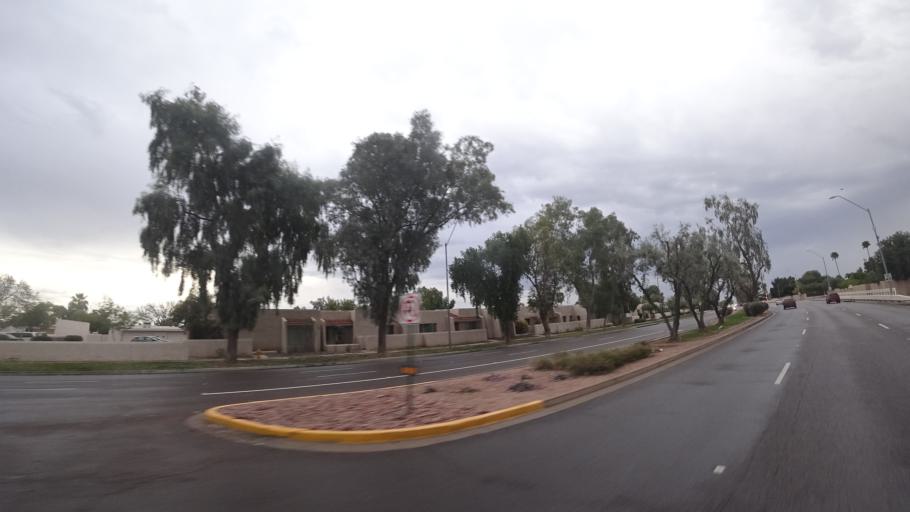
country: US
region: Arizona
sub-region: Maricopa County
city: Scottsdale
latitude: 33.5417
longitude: -111.9086
